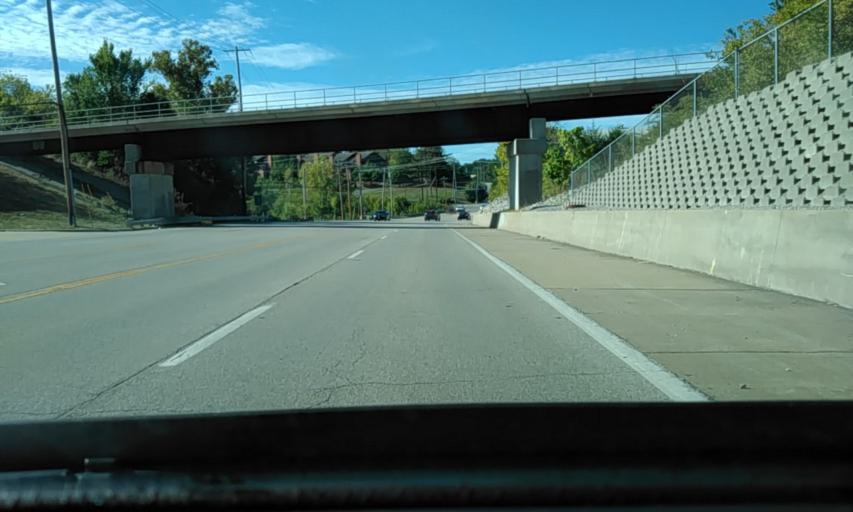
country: US
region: Missouri
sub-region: Saint Louis County
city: Mehlville
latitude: 38.4961
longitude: -90.3430
